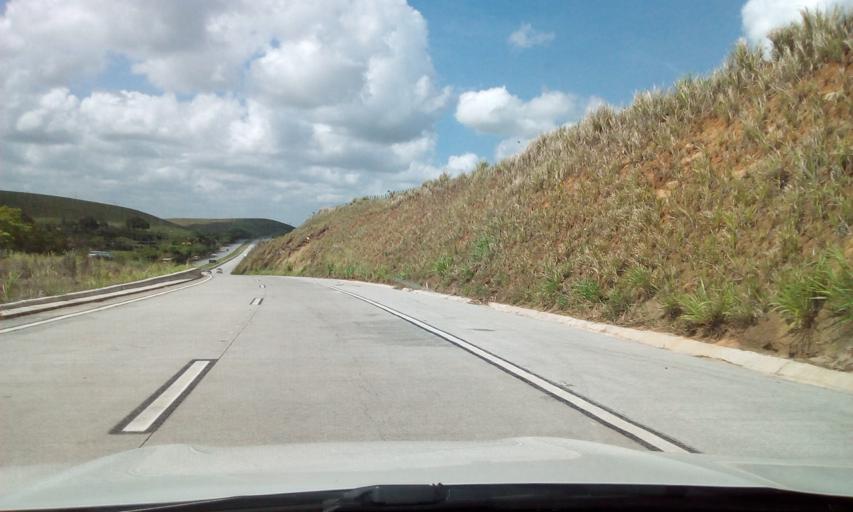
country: BR
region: Alagoas
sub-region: Flexeiras
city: Flexeiras
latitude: -9.2544
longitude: -35.7732
